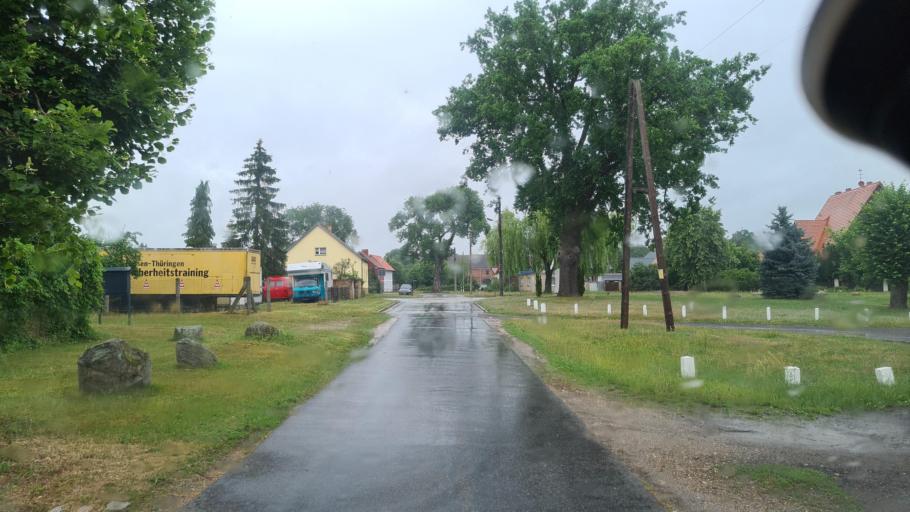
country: DE
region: Brandenburg
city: Juterbog
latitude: 51.9845
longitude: 13.1723
